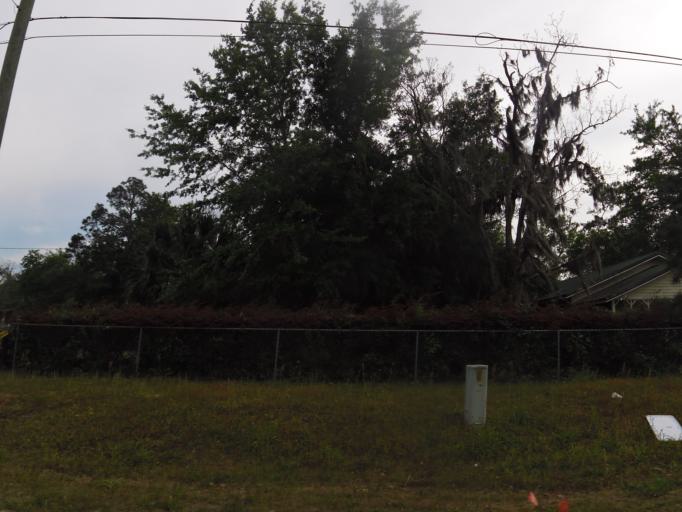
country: US
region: Florida
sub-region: Nassau County
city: Hilliard
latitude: 30.6975
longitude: -81.9087
